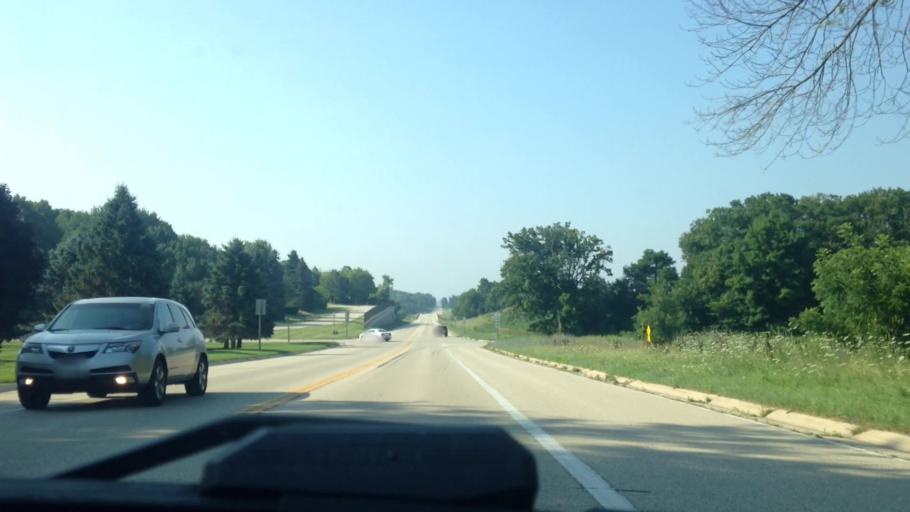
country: US
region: Wisconsin
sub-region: Washington County
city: Slinger
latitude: 43.3175
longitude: -88.2608
